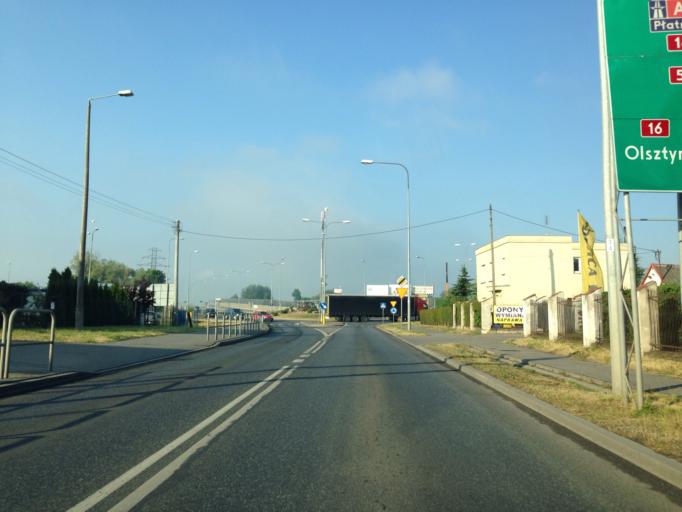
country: PL
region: Kujawsko-Pomorskie
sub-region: Grudziadz
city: Grudziadz
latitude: 53.5046
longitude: 18.7996
